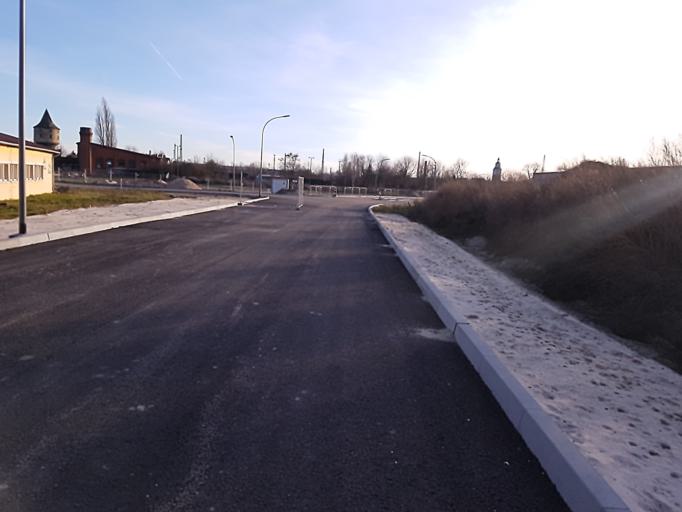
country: DE
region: Brandenburg
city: Finsterwalde
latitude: 51.6415
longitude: 13.7143
